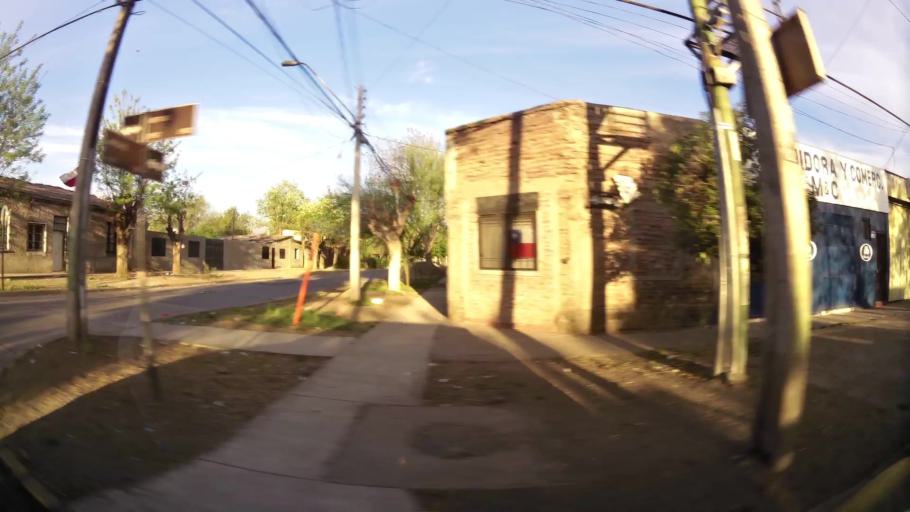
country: CL
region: Santiago Metropolitan
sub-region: Provincia de Santiago
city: Lo Prado
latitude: -33.4287
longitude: -70.7197
